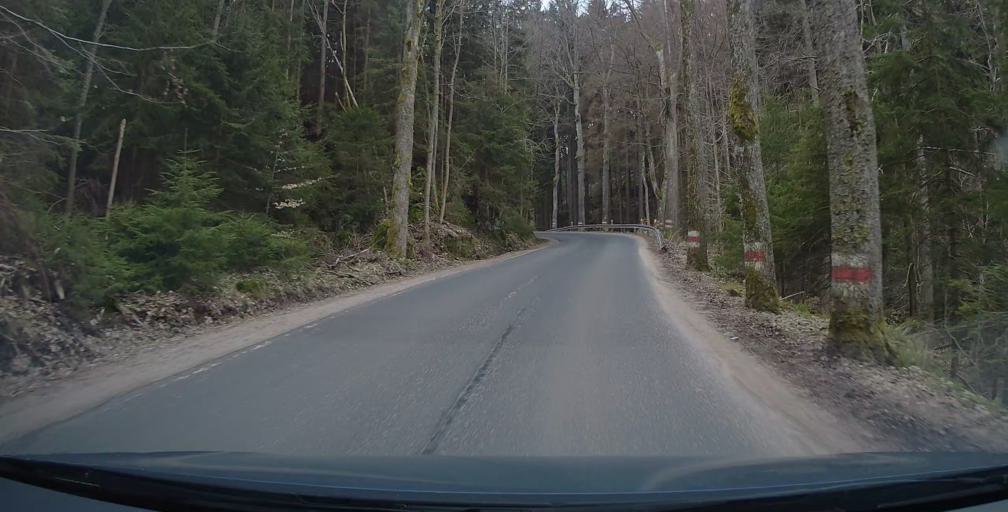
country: PL
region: Lower Silesian Voivodeship
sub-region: Powiat klodzki
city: Radkow
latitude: 50.4772
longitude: 16.3940
